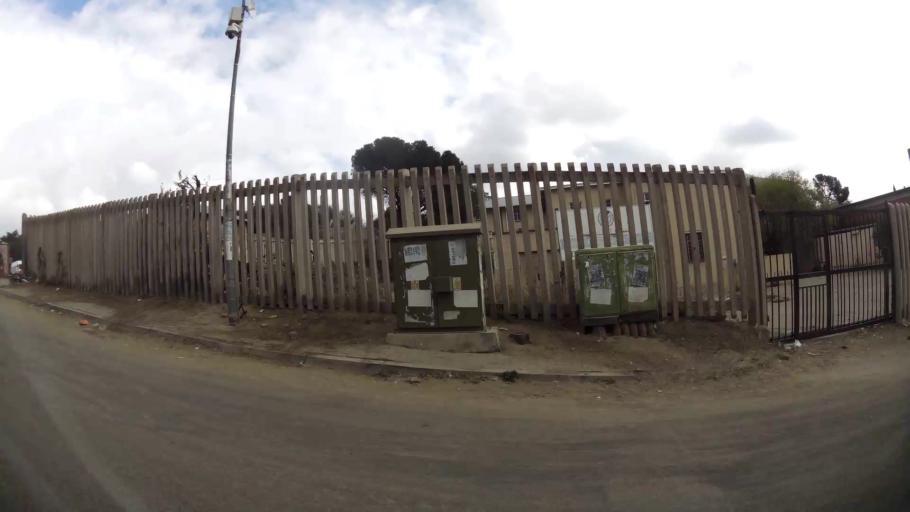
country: ZA
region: Orange Free State
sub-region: Mangaung Metropolitan Municipality
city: Bloemfontein
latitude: -29.1229
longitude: 26.2230
